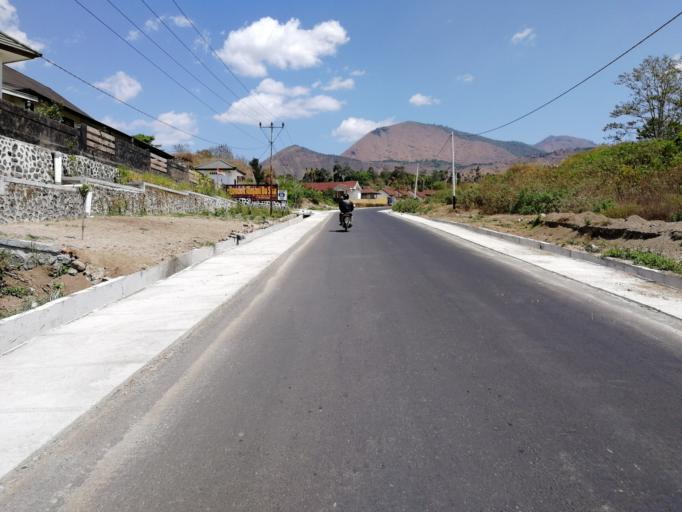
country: ID
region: West Nusa Tenggara
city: Sembalunlawang
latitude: -8.3546
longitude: 116.5136
